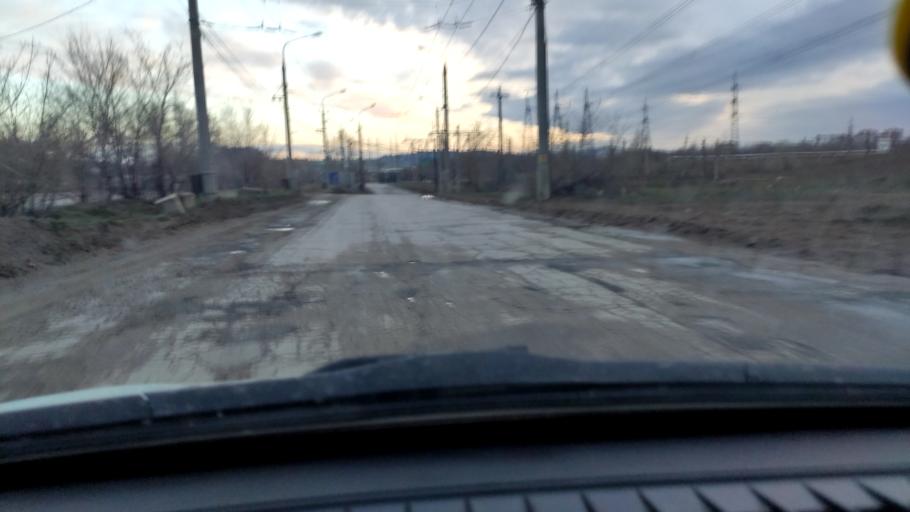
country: RU
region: Samara
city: Zhigulevsk
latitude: 53.4880
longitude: 49.5097
